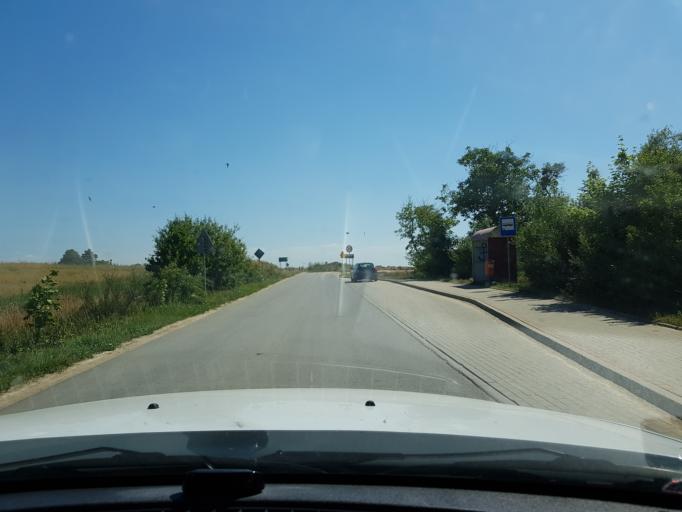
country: PL
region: West Pomeranian Voivodeship
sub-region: Powiat koszalinski
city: Mielno
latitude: 54.1939
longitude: 16.0557
